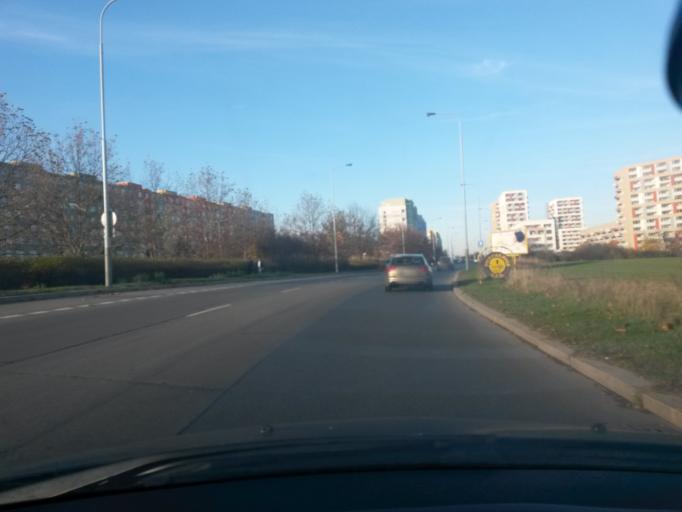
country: CZ
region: Central Bohemia
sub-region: Okres Praha-Zapad
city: Pruhonice
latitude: 50.0373
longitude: 14.5667
